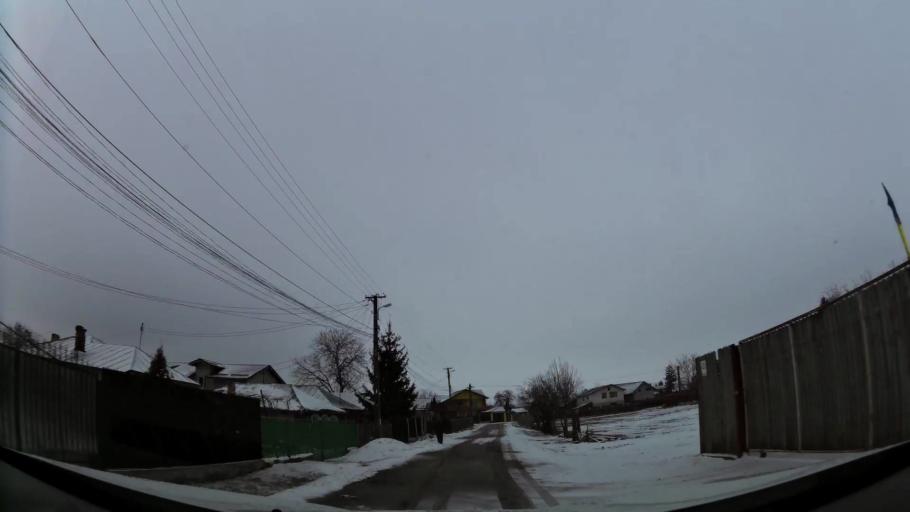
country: RO
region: Prahova
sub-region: Comuna Berceni
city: Corlatesti
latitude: 44.9154
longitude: 26.0847
